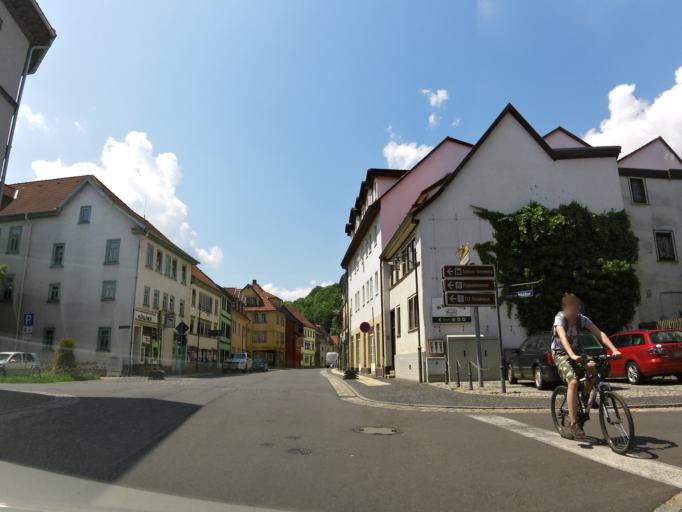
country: DE
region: Thuringia
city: Waltershausen
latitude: 50.8977
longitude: 10.5540
